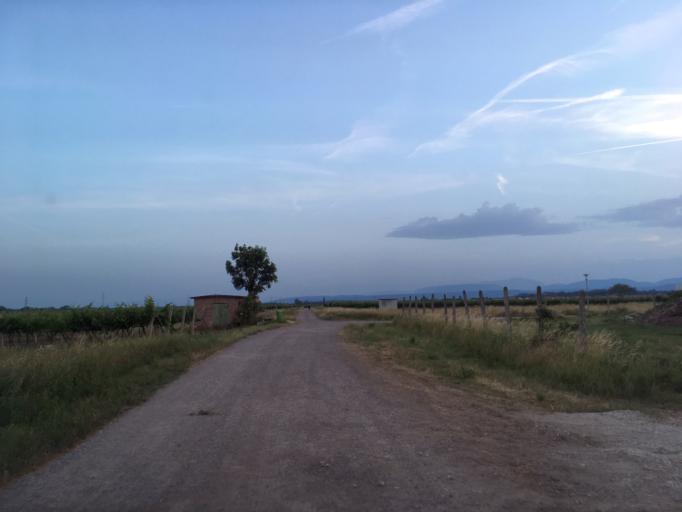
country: AT
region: Lower Austria
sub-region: Politischer Bezirk Baden
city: Teesdorf
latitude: 47.9457
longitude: 16.2849
